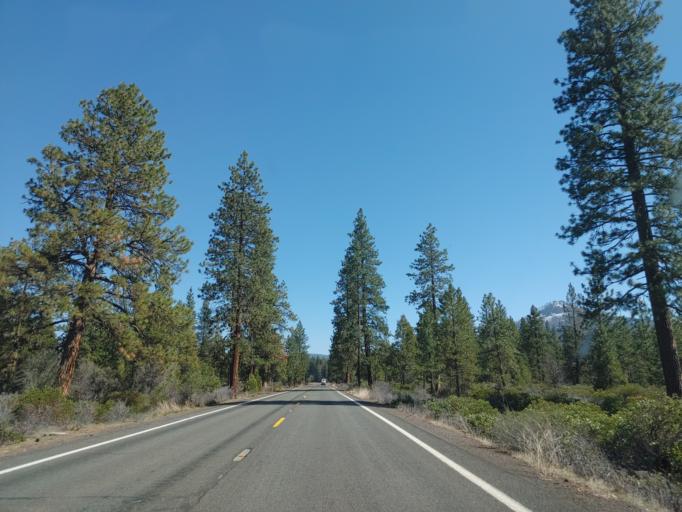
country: US
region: California
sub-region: Shasta County
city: Burney
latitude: 40.7493
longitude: -121.4854
